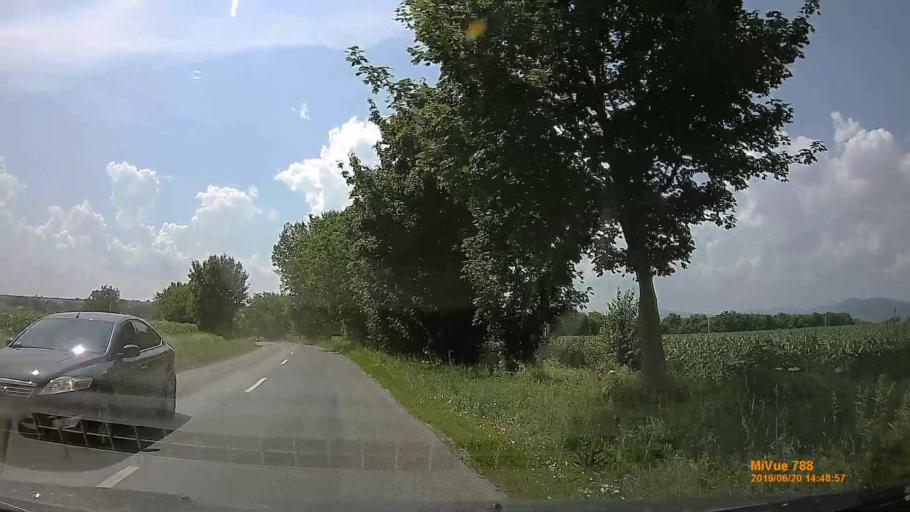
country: HU
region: Baranya
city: Kozarmisleny
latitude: 46.0164
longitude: 18.2812
